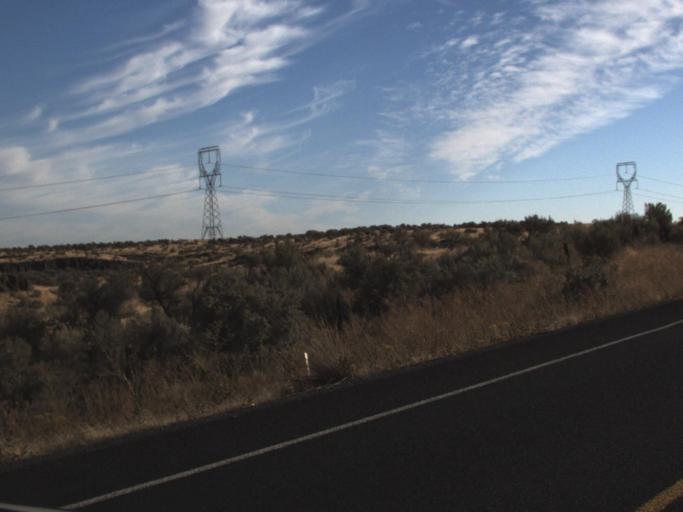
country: US
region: Washington
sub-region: Franklin County
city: Connell
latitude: 46.6316
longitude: -118.7514
